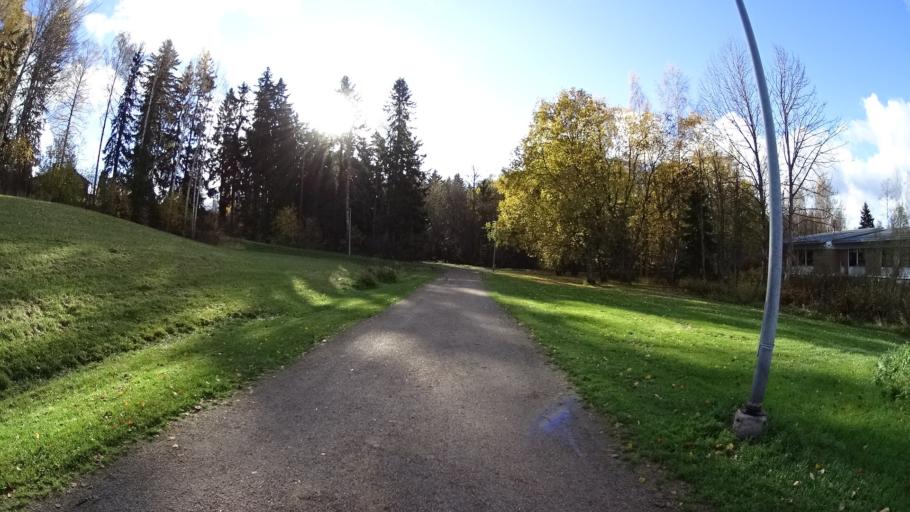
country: FI
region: Uusimaa
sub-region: Helsinki
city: Kilo
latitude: 60.2721
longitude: 24.8173
